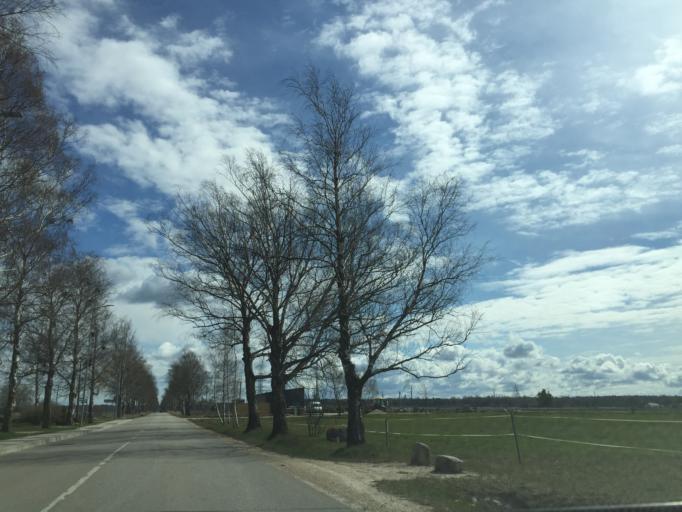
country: LV
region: Salacgrivas
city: Salacgriva
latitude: 57.7485
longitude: 24.3700
